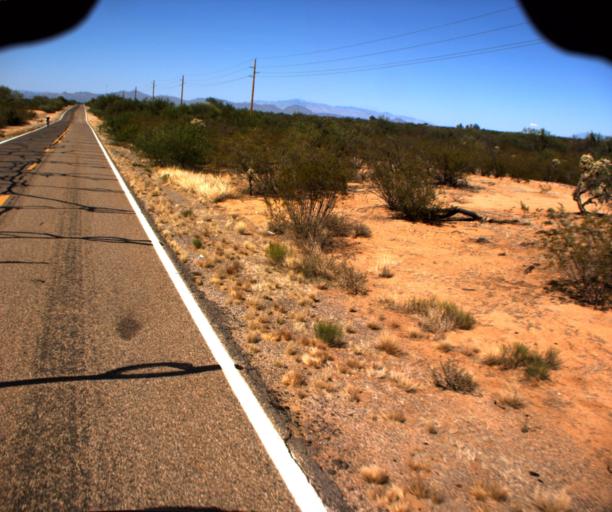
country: US
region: Arizona
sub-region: Pima County
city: Three Points
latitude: 32.0412
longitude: -111.3345
